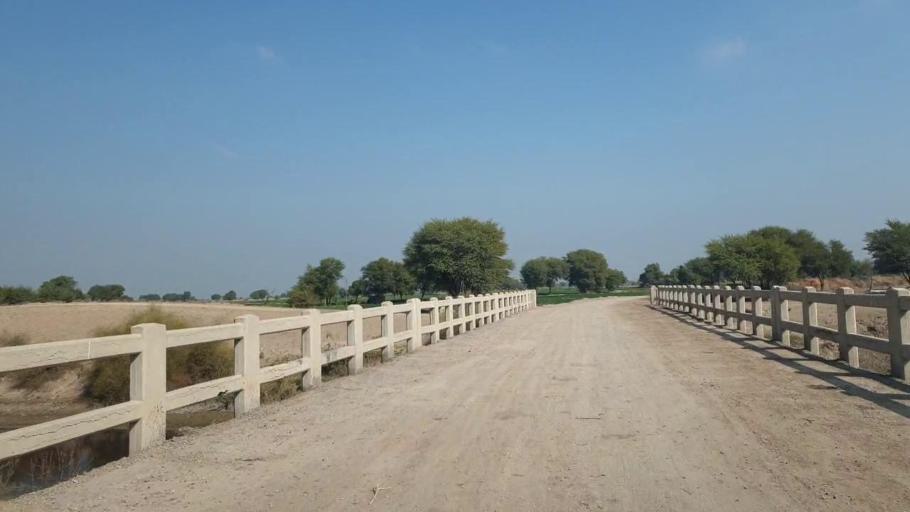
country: PK
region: Sindh
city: Shahdadpur
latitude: 26.0298
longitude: 68.6153
